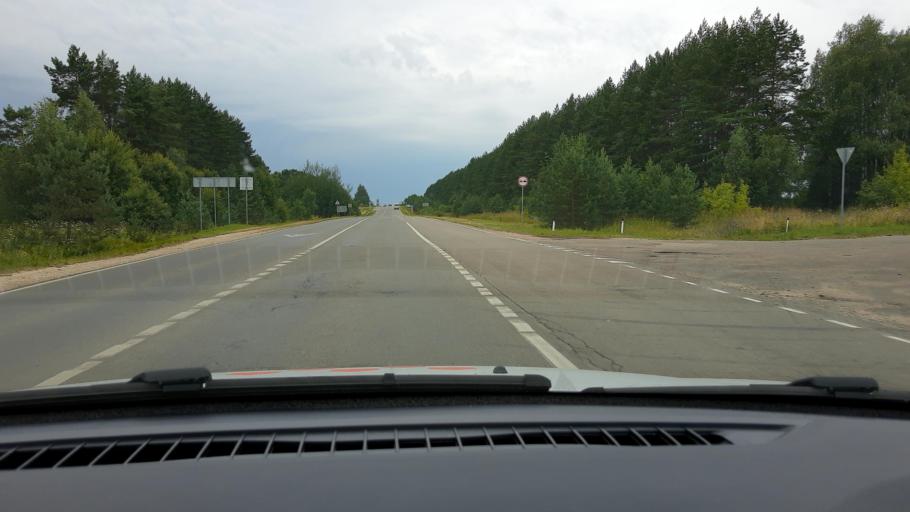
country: RU
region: Nizjnij Novgorod
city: Vyyezdnoye
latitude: 55.1546
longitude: 43.5744
